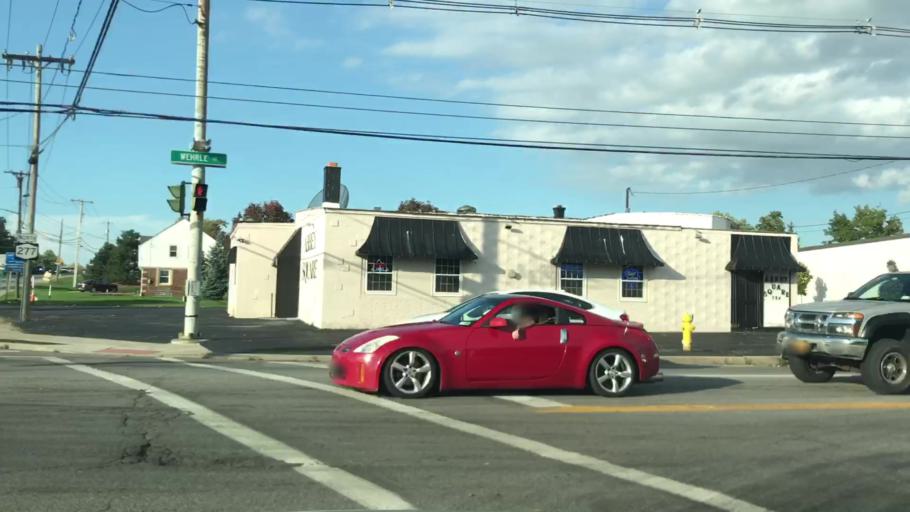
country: US
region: New York
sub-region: Erie County
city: Williamsville
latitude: 42.9495
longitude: -78.7545
